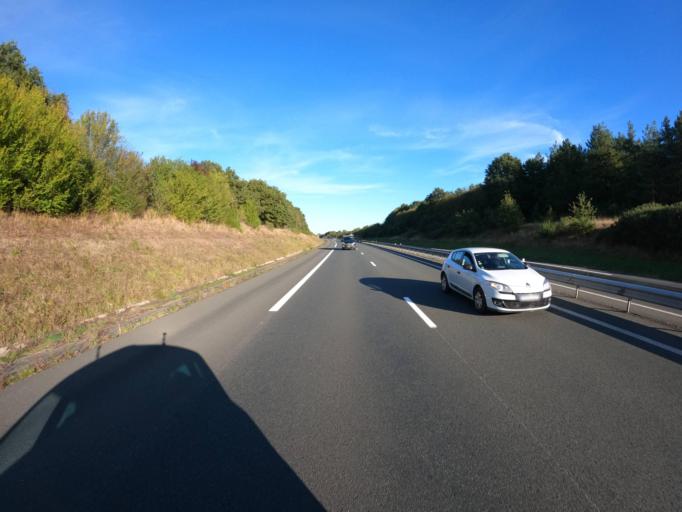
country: FR
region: Pays de la Loire
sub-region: Departement de Maine-et-Loire
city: Saint-Lambert-du-Lattay
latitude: 47.2413
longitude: -0.6508
